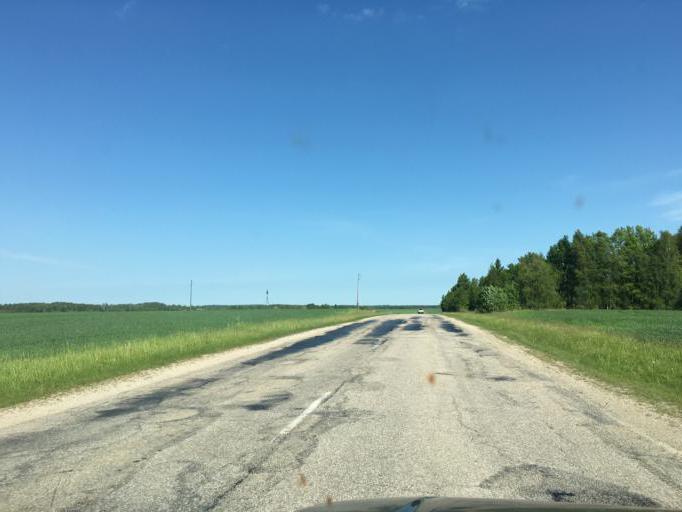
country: LV
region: Talsu Rajons
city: Valdemarpils
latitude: 57.3610
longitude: 22.4913
